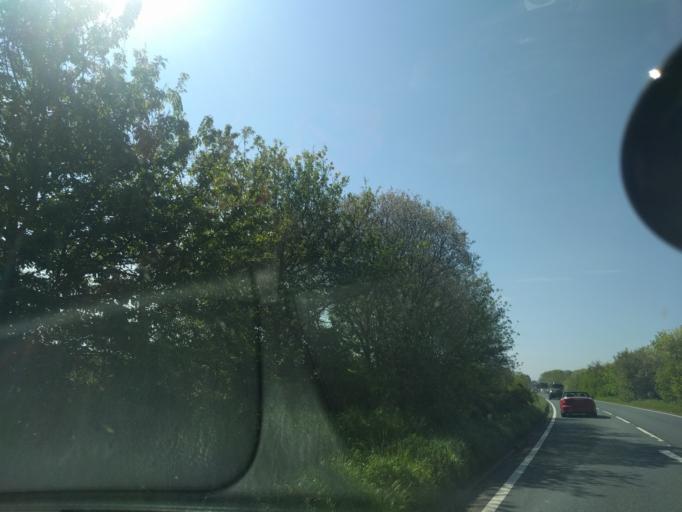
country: GB
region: England
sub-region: Somerset
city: Ilchester
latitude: 51.0284
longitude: -2.6626
